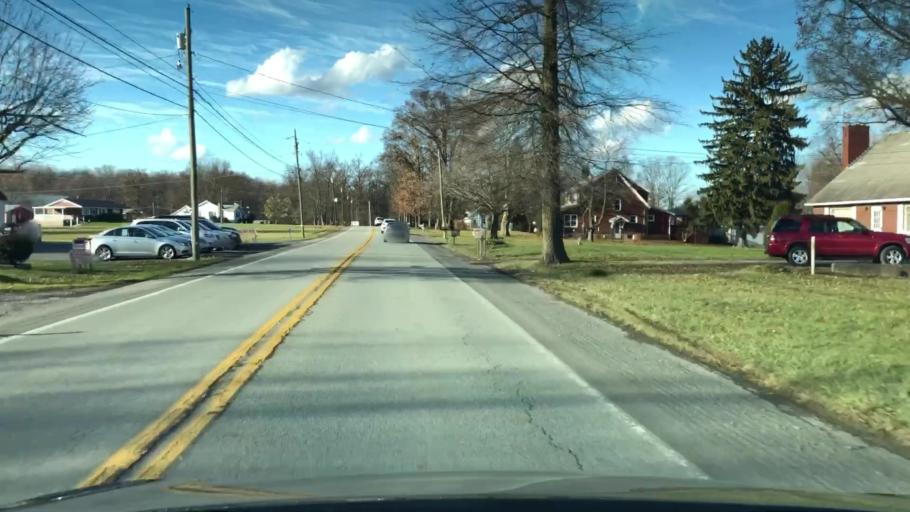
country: US
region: Pennsylvania
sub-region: Butler County
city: Saxonburg
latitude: 40.7464
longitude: -79.7691
